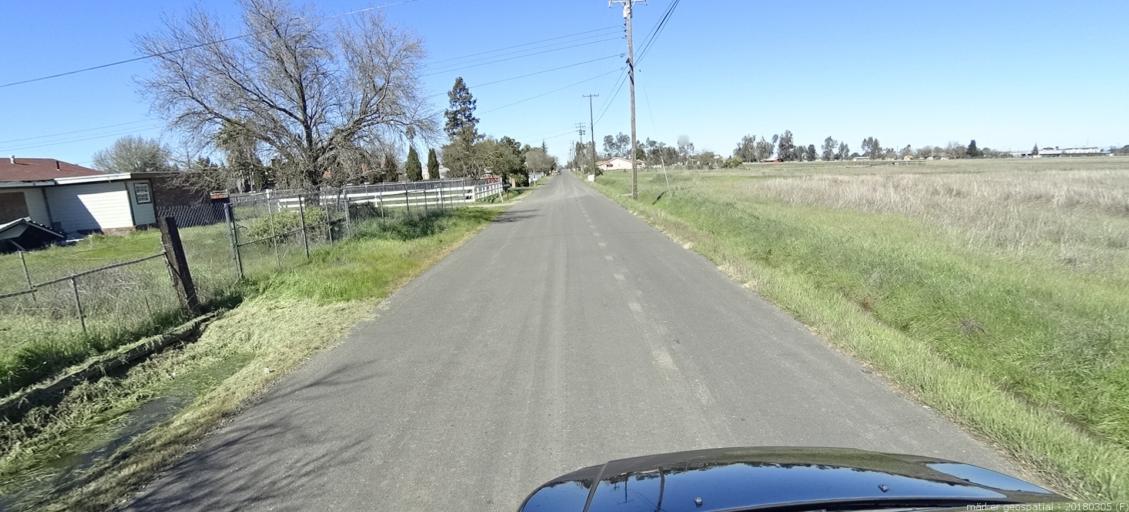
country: US
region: California
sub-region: Sacramento County
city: Florin
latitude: 38.4901
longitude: -121.3789
